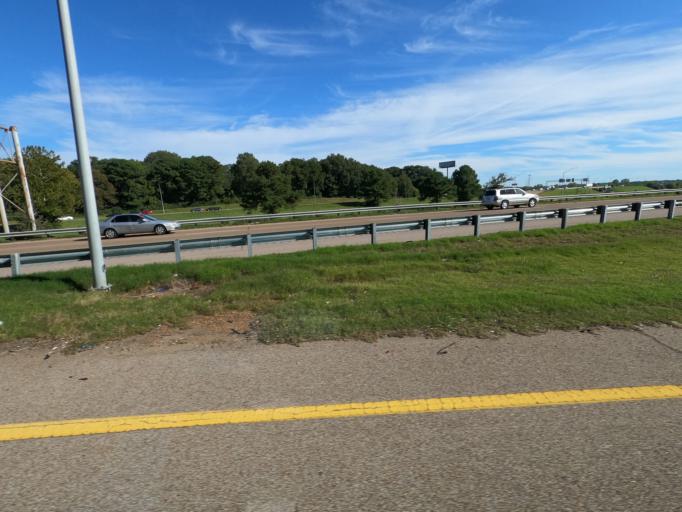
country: US
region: Tennessee
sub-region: Shelby County
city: New South Memphis
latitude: 35.0761
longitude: -90.0271
